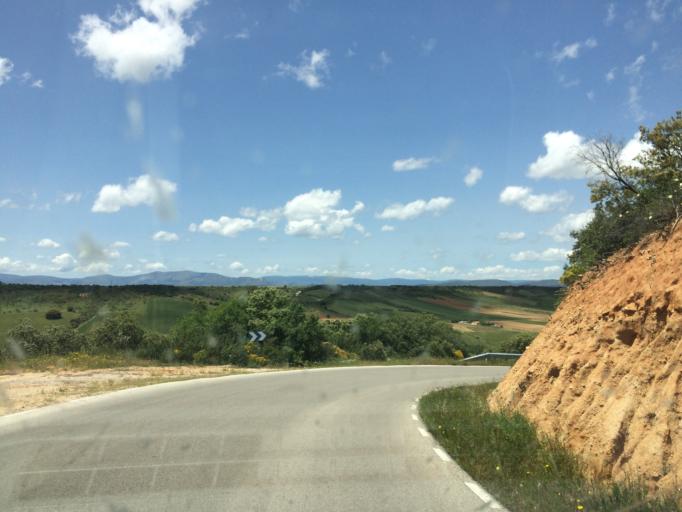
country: ES
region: Madrid
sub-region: Provincia de Madrid
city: Valdepielagos
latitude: 40.7560
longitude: -3.4146
